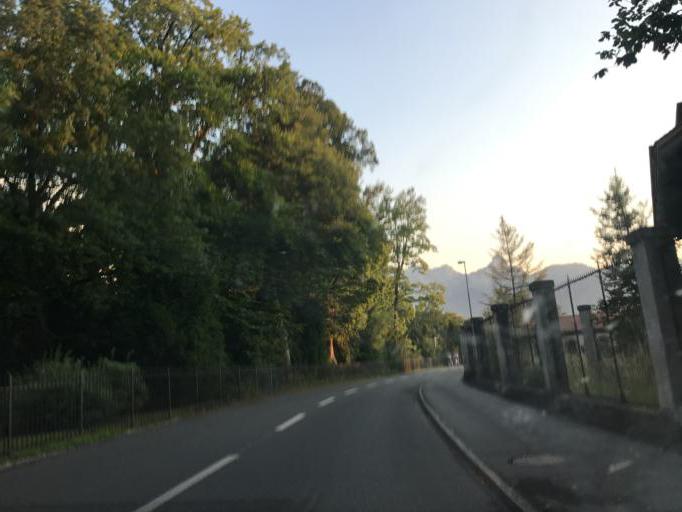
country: CH
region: Bern
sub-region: Thun District
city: Thun
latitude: 46.7470
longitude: 7.6362
